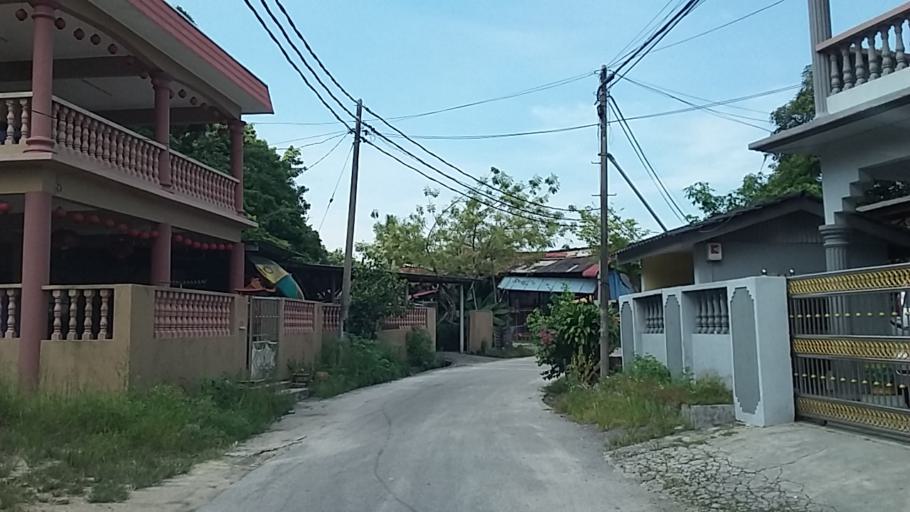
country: MY
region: Johor
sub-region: Daerah Batu Pahat
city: Batu Pahat
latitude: 1.7869
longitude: 102.8936
